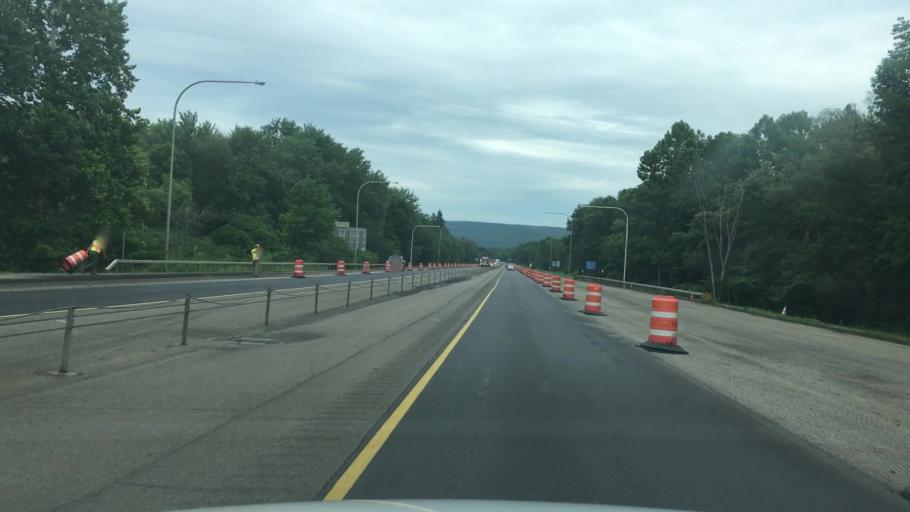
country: US
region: New York
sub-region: Otsego County
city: Oneonta
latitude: 42.4512
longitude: -75.0473
